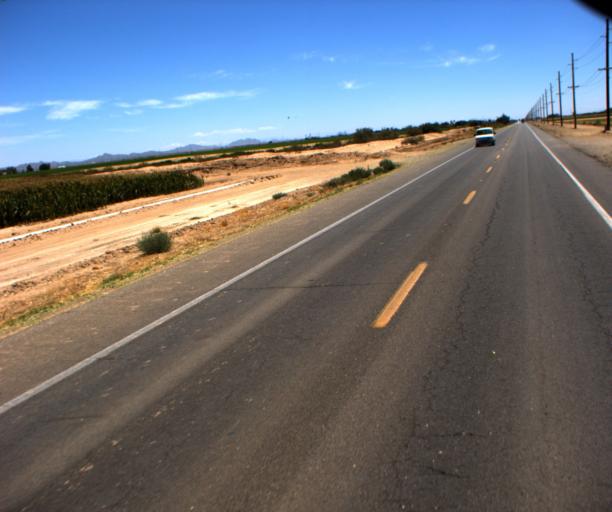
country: US
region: Arizona
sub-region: Pinal County
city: Maricopa
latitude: 32.8793
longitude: -111.9898
